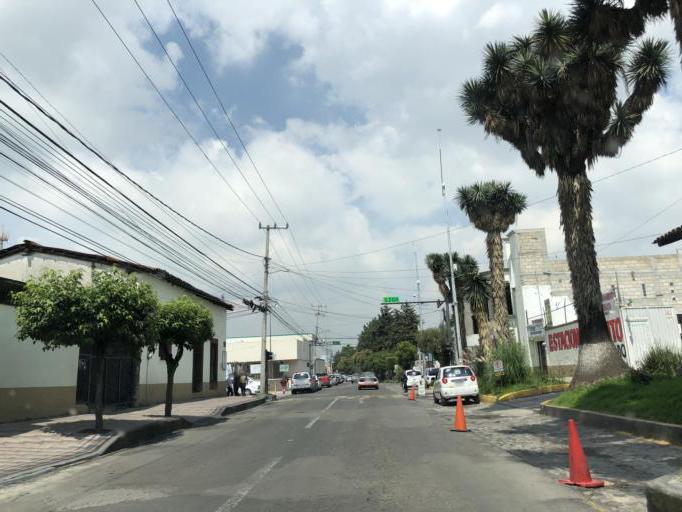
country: MX
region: Morelos
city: Lerma de Villada
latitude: 19.2867
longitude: -99.5150
